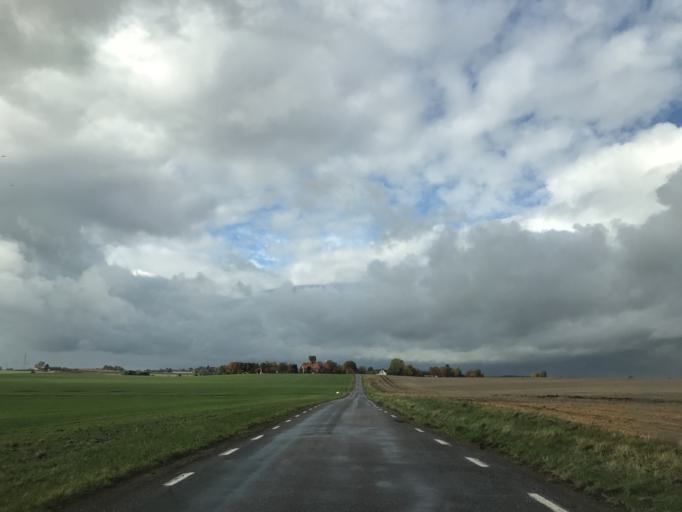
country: SE
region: Skane
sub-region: Svalovs Kommun
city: Svaloev
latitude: 55.9085
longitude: 13.1548
